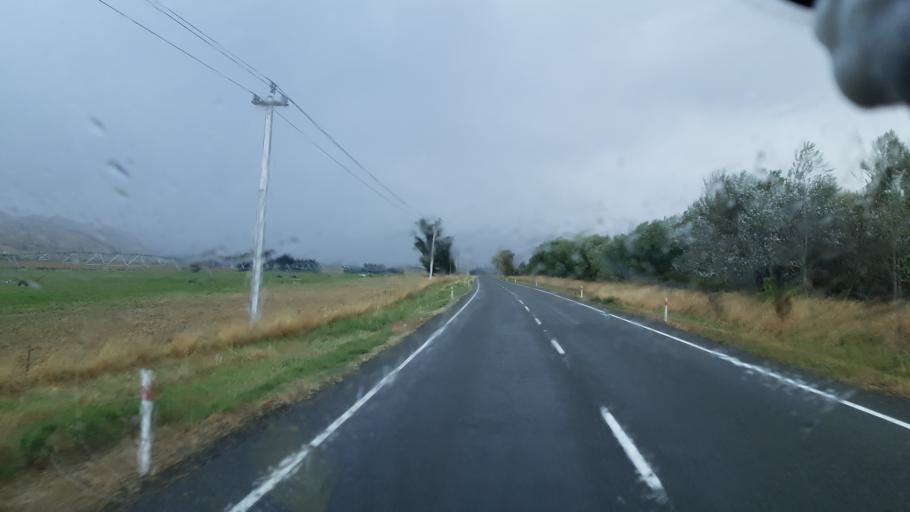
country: NZ
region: Canterbury
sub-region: Hurunui District
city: Amberley
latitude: -42.7074
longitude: 172.8392
